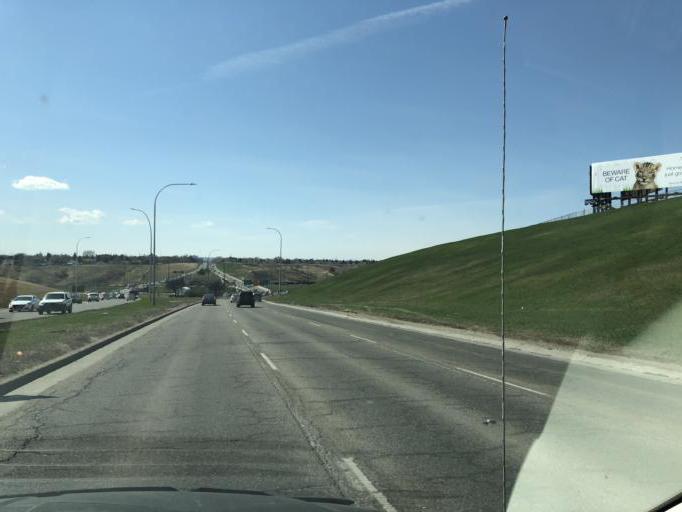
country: CA
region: Alberta
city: Calgary
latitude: 51.0670
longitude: -114.0185
